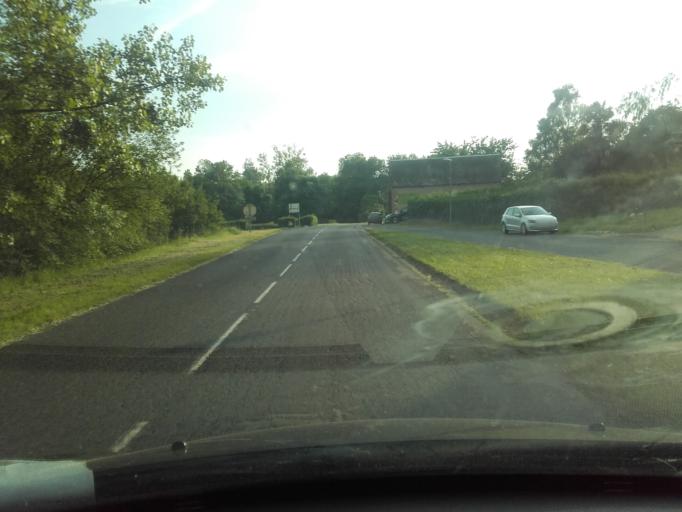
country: FR
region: Centre
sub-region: Departement d'Indre-et-Loire
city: Noizay
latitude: 47.4186
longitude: 0.8747
